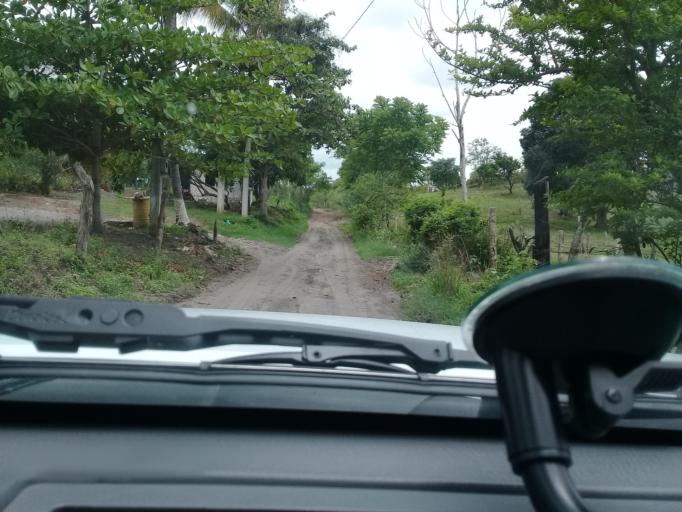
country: MX
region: Veracruz
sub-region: Paso de Ovejas
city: El Hatito
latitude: 19.2747
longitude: -96.3987
